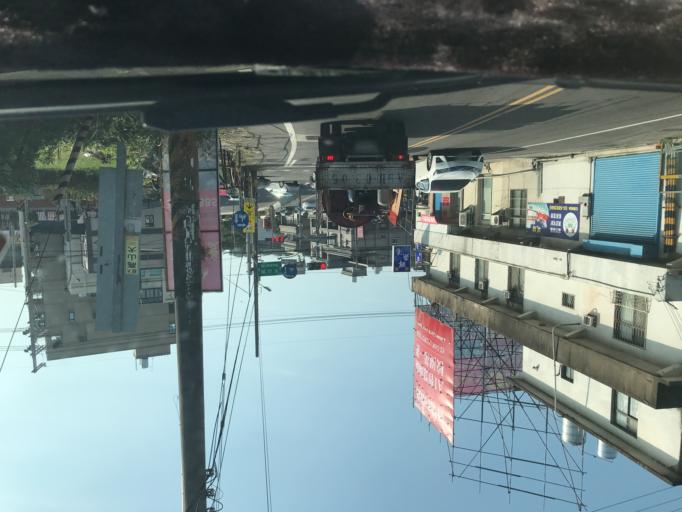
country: TW
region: Taiwan
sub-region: Hsinchu
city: Zhubei
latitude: 24.8313
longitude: 121.0364
